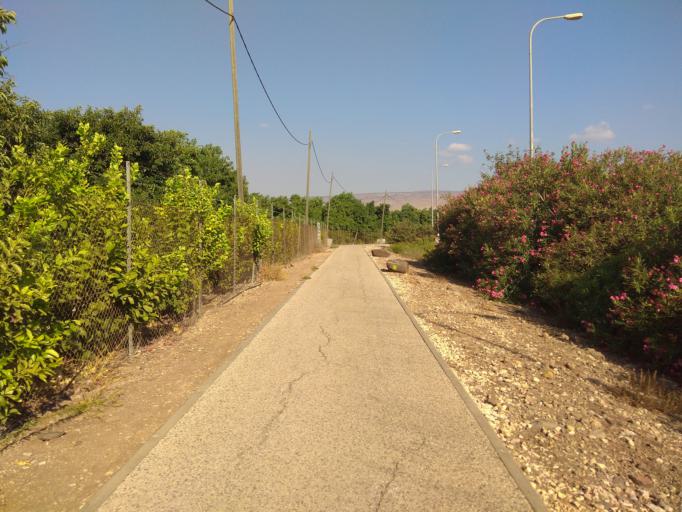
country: IL
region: Northern District
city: Qiryat Shemona
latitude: 33.2253
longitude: 35.6232
